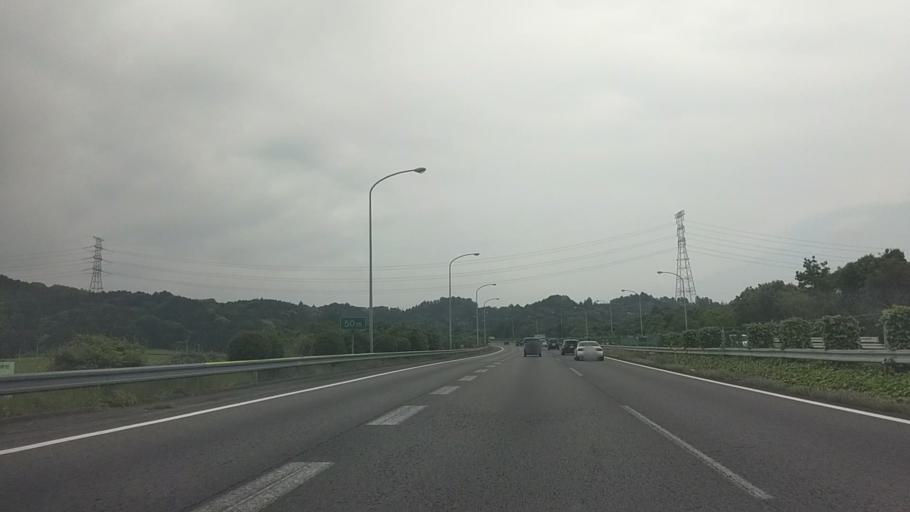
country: JP
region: Shizuoka
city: Kanaya
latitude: 34.7553
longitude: 138.1192
